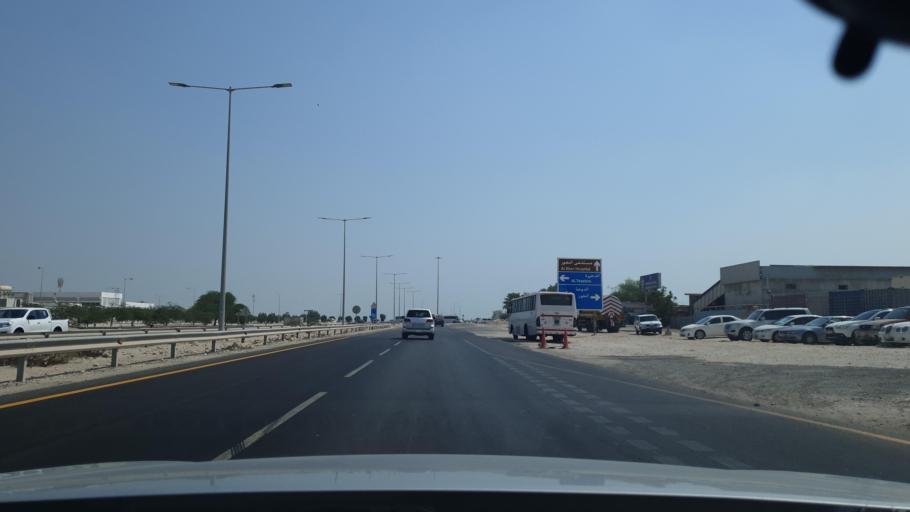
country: QA
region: Al Khawr
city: Al Khawr
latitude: 25.7156
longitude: 51.5061
